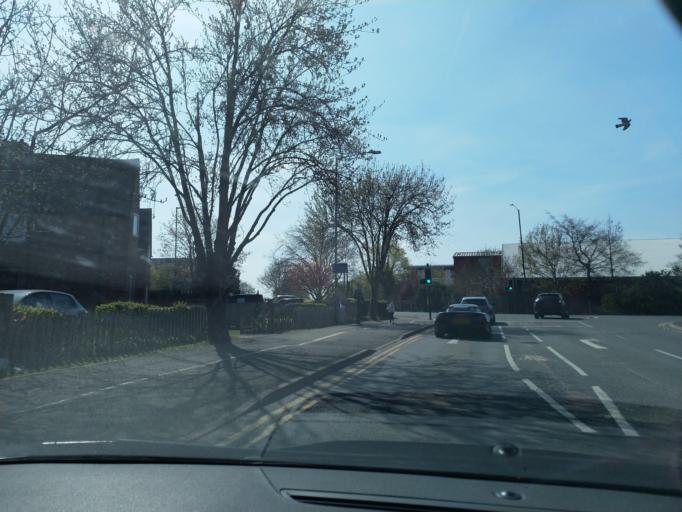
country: GB
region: England
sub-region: Warwickshire
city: Stratford-upon-Avon
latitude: 52.1948
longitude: -1.7195
